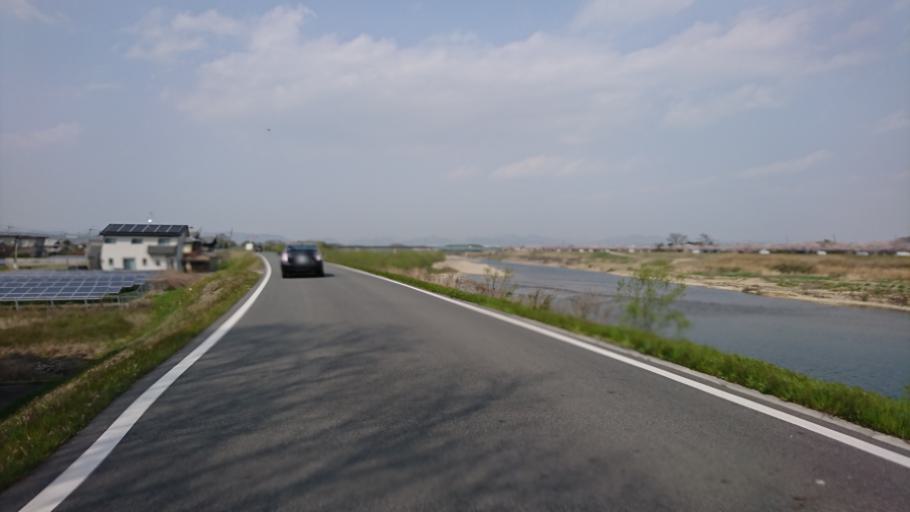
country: JP
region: Hyogo
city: Ono
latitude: 34.8711
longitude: 134.9227
